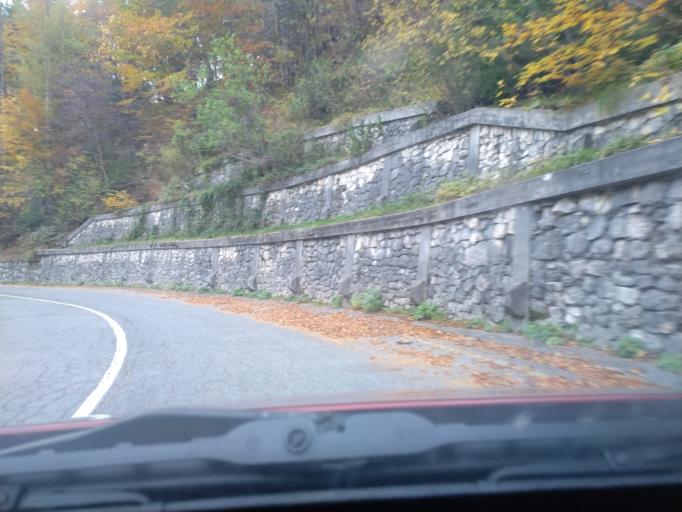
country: SI
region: Kranjska Gora
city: Kranjska Gora
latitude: 46.4048
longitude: 13.7384
